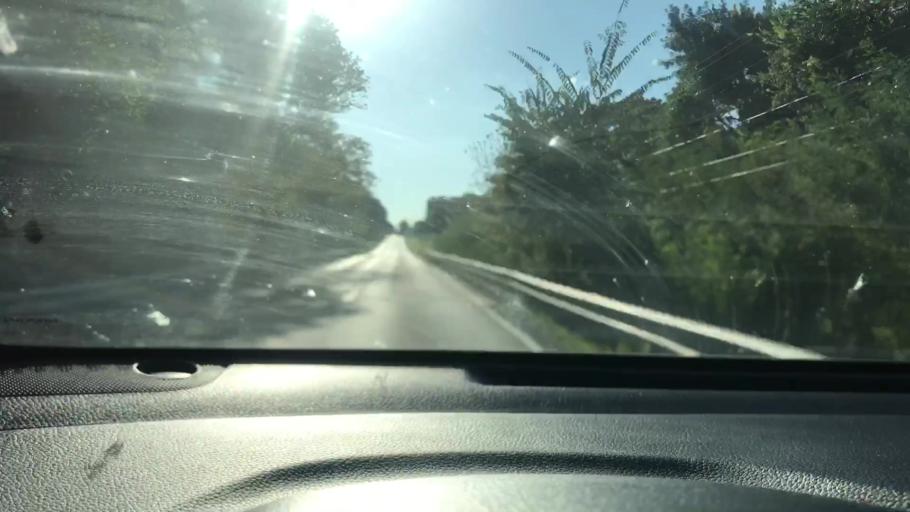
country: US
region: Kentucky
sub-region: Calloway County
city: Murray
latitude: 36.5804
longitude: -88.2527
